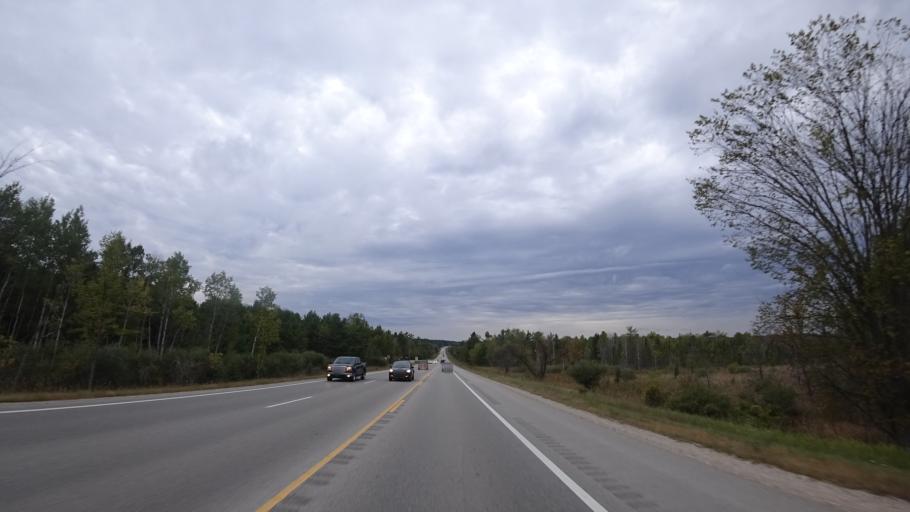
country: US
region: Michigan
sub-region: Kalkaska County
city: Rapid City
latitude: 44.7777
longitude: -85.3564
